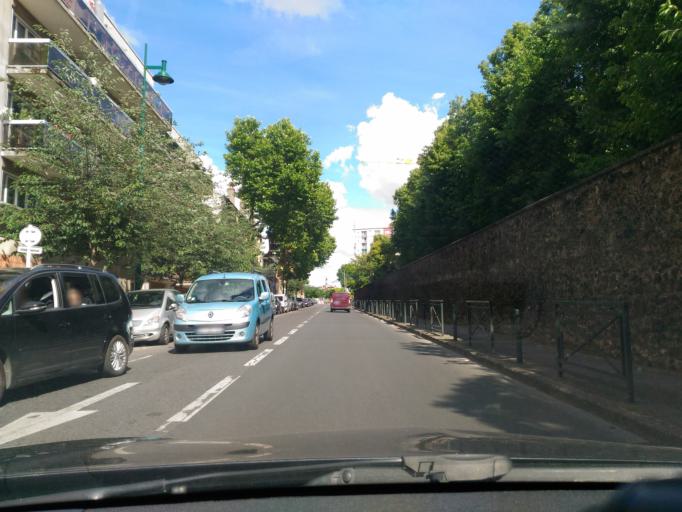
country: FR
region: Ile-de-France
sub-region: Departement des Hauts-de-Seine
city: Montrouge
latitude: 48.8101
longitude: 2.3145
